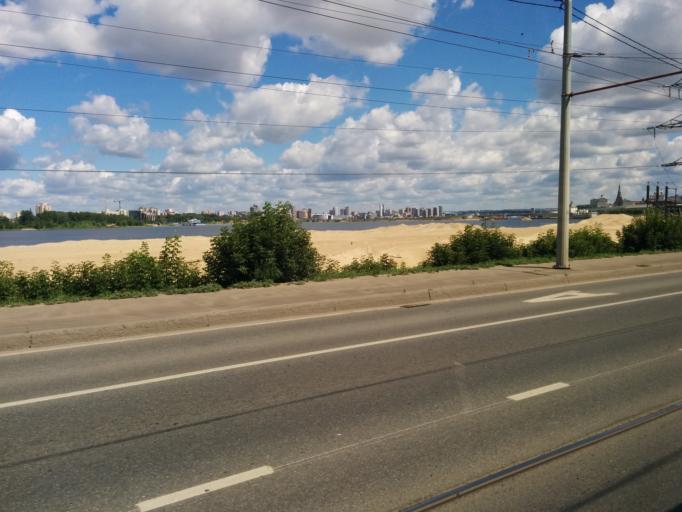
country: RU
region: Tatarstan
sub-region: Gorod Kazan'
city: Kazan
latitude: 55.7976
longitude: 49.0813
